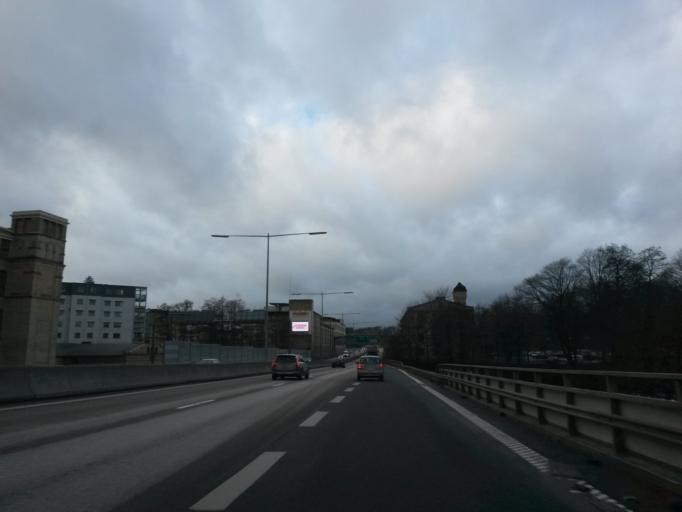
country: SE
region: Vaestra Goetaland
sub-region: Boras Kommun
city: Boras
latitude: 57.7160
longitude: 12.9399
